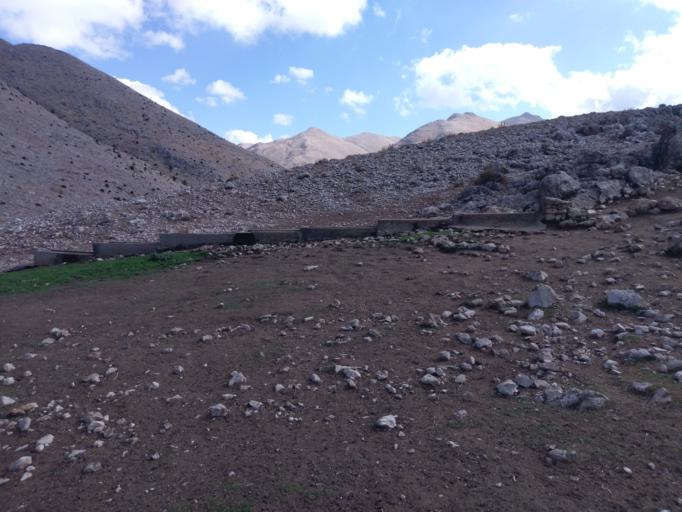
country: TR
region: Kayseri
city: Toklar
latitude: 38.4303
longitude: 36.1647
